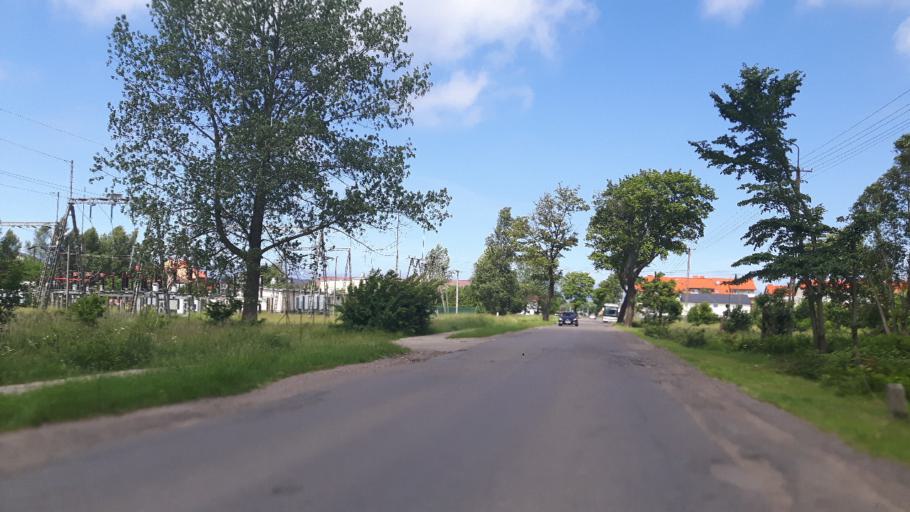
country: PL
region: Pomeranian Voivodeship
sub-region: Powiat slupski
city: Ustka
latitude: 54.5703
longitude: 16.8507
